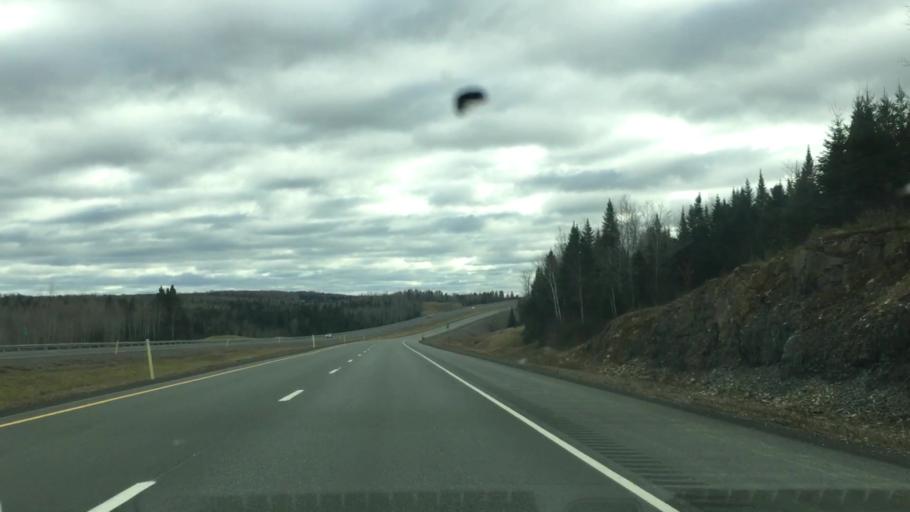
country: CA
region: New Brunswick
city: Florenceville-Bristol
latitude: 46.5429
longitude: -67.7169
